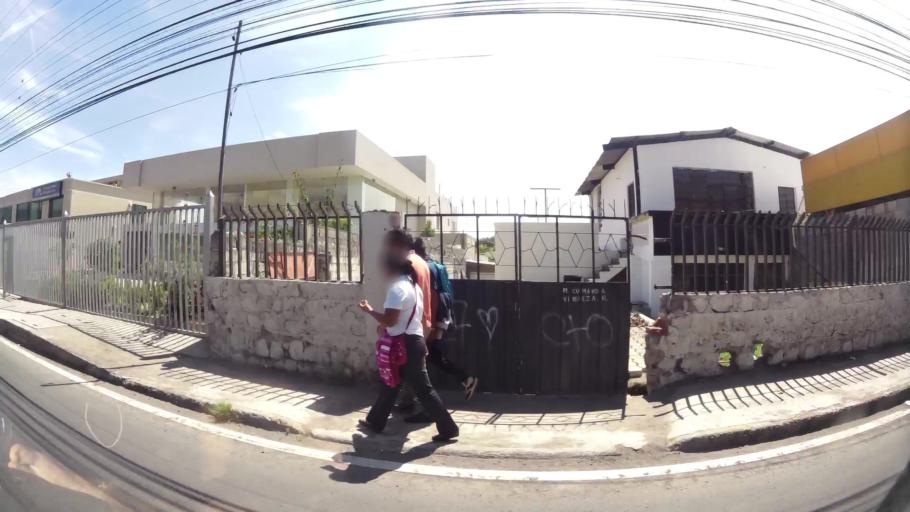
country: EC
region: Pichincha
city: Quito
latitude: -0.2132
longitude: -78.4097
